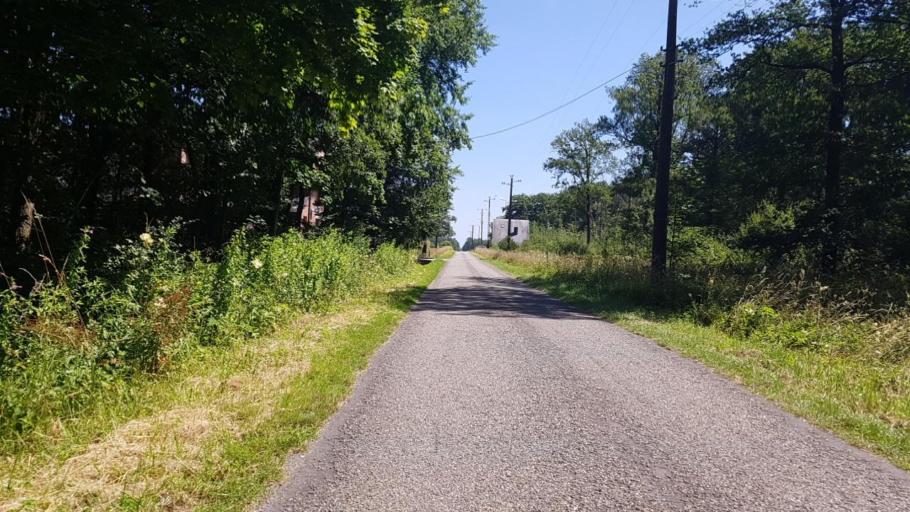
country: BE
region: Wallonia
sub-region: Province du Hainaut
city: Froidchapelle
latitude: 50.1130
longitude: 4.2440
